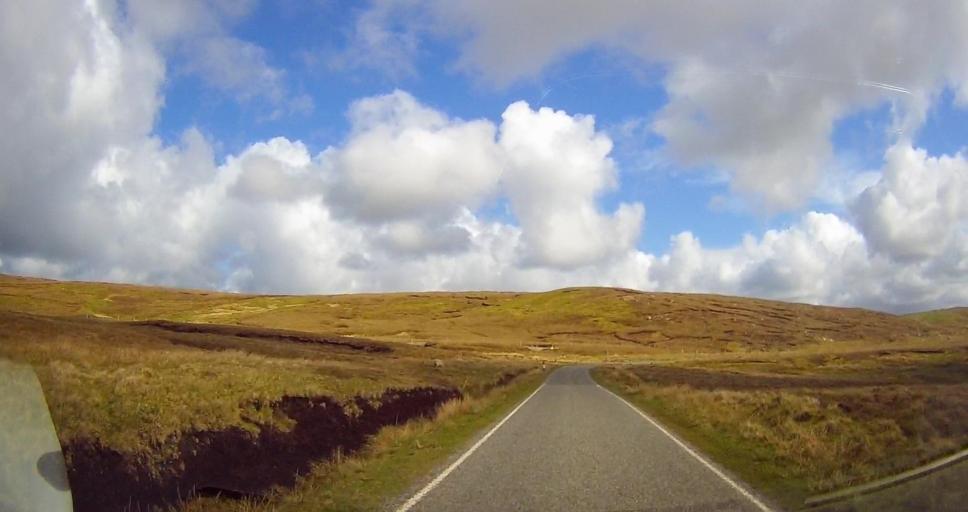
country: GB
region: Scotland
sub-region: Shetland Islands
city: Lerwick
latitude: 60.4961
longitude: -1.3942
